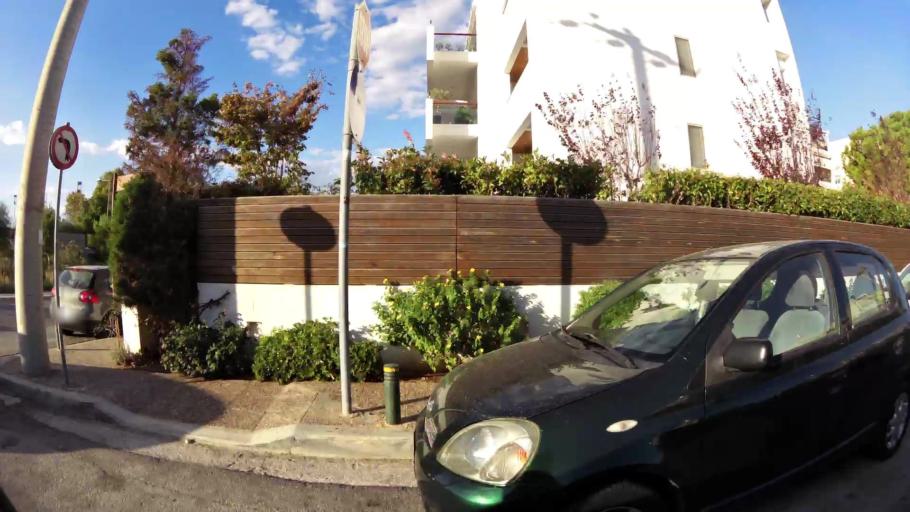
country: GR
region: Attica
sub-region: Nomarchia Athinas
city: Elliniko
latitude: 37.8882
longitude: 23.7460
